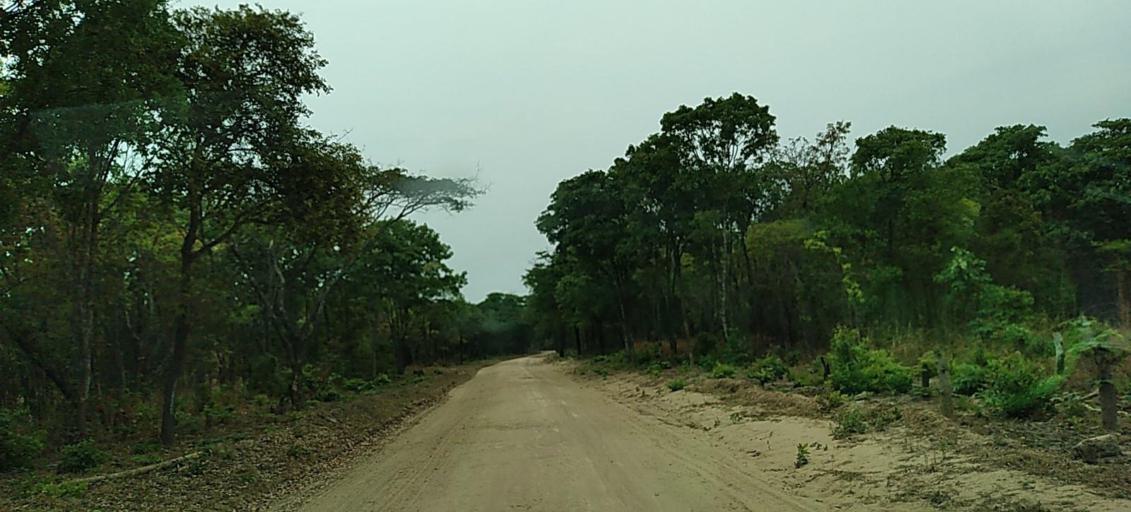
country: ZM
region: North-Western
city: Solwezi
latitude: -12.5310
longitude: 26.5230
